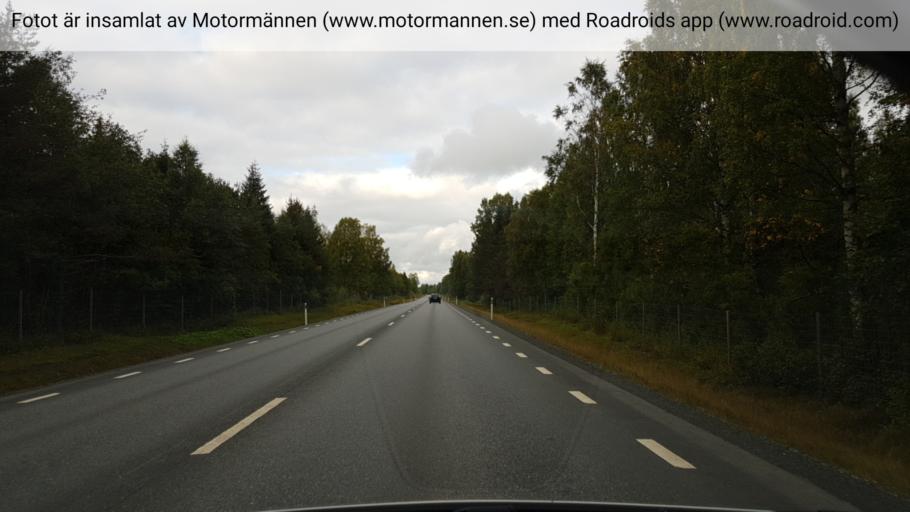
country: SE
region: Vaesterbotten
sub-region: Skelleftea Kommun
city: Forsbacka
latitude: 64.8097
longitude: 20.6440
